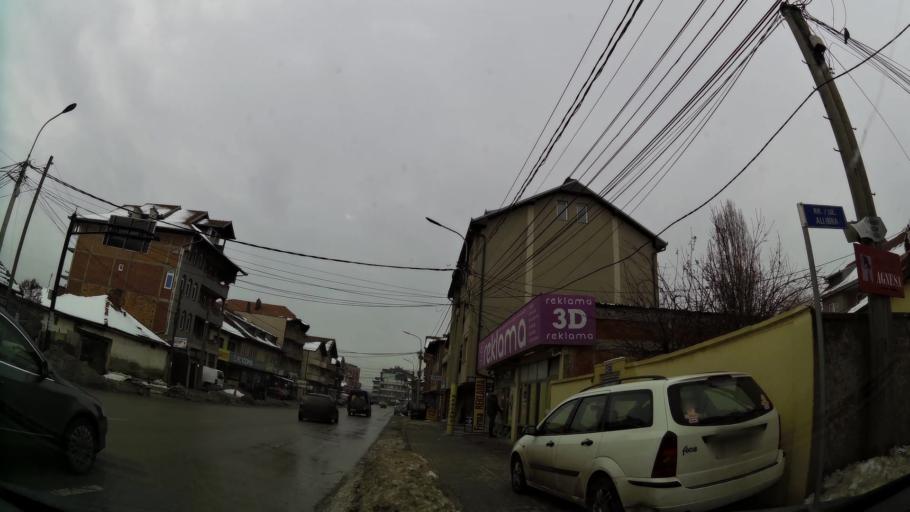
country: XK
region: Pristina
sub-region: Komuna e Prishtines
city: Pristina
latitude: 42.6796
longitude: 21.1604
